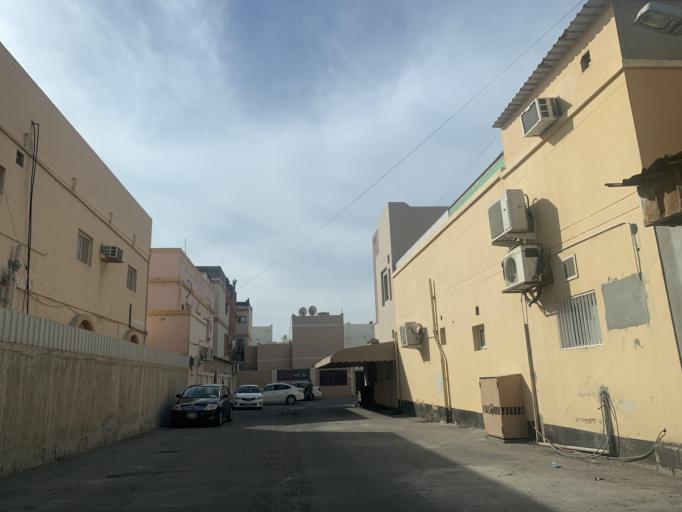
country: BH
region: Central Governorate
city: Madinat Hamad
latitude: 26.1223
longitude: 50.4768
